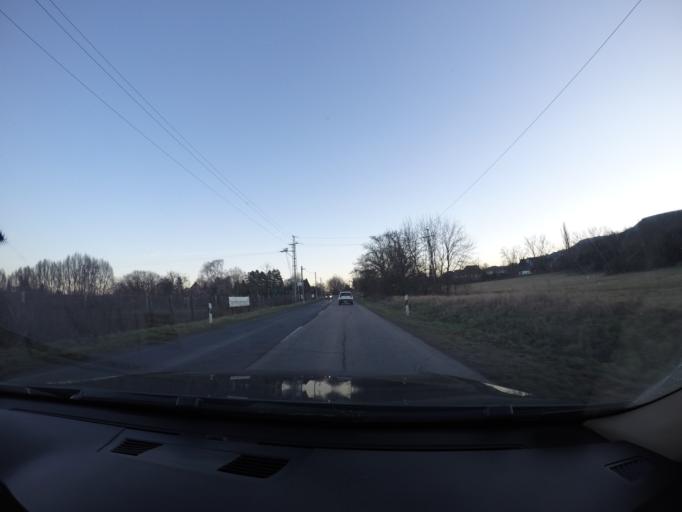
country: HU
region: Pest
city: Dunabogdany
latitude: 47.7657
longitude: 19.0646
